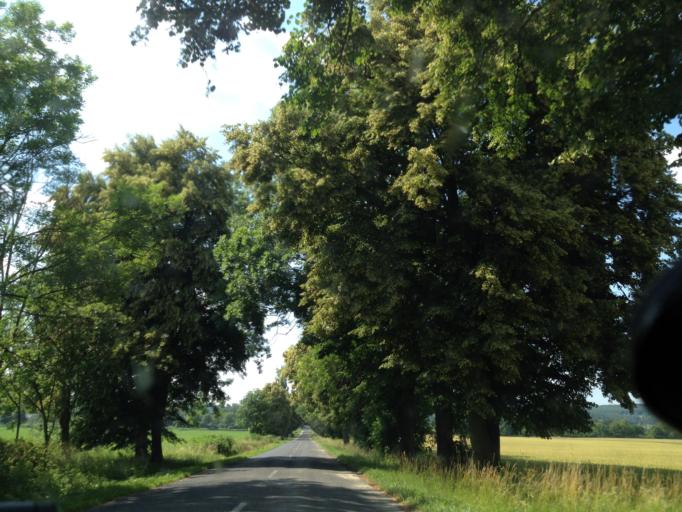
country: HU
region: Veszprem
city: Urkut
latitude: 47.0708
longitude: 17.6890
